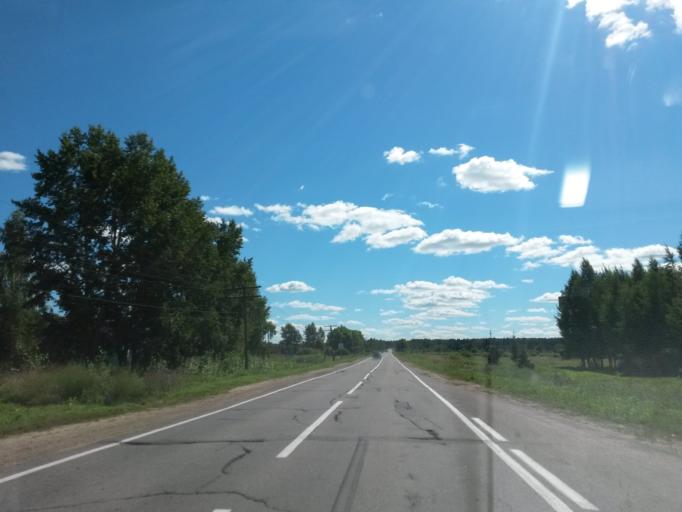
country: RU
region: Jaroslavl
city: Tutayev
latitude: 57.9376
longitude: 39.4996
